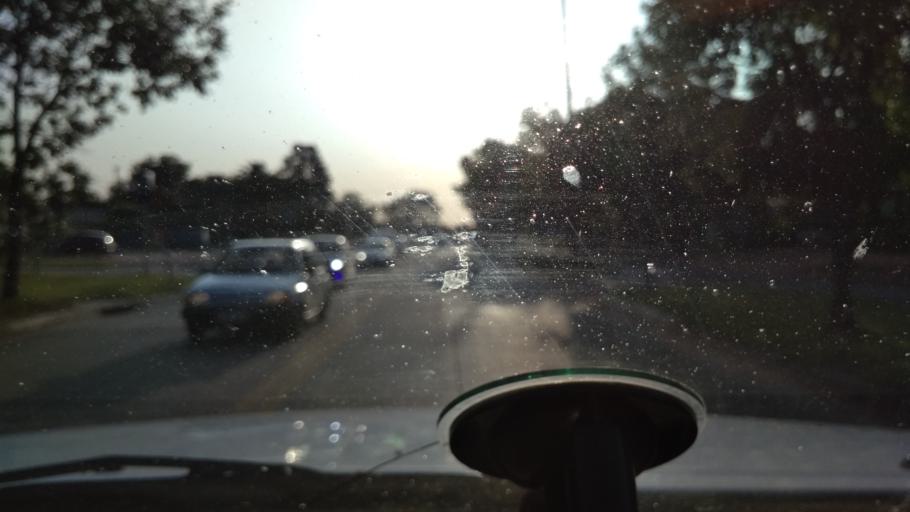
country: UY
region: Canelones
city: Paso de Carrasco
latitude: -34.8695
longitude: -56.0679
